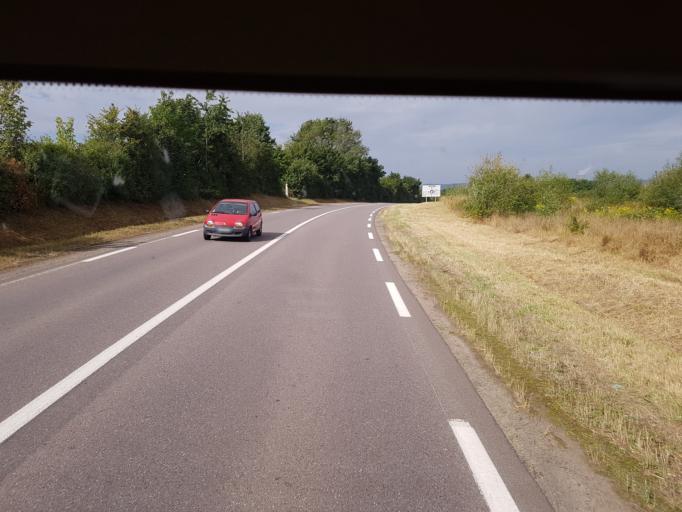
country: FR
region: Lorraine
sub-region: Departement de la Moselle
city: Koenigsmacker
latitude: 49.4063
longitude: 6.3019
